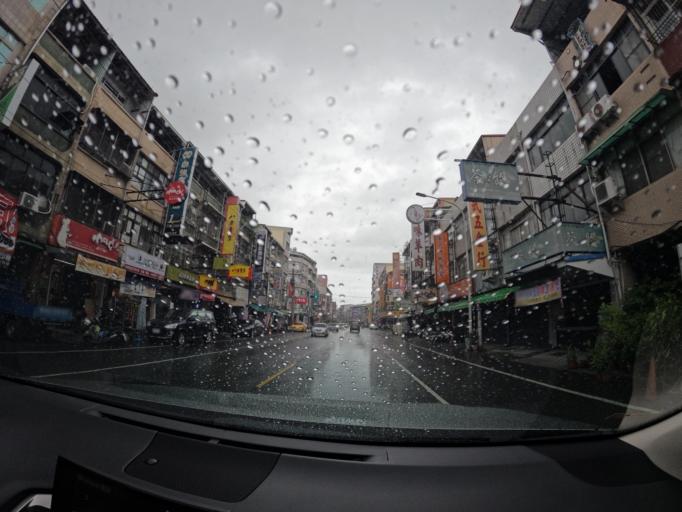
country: TW
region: Taiwan
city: Fengshan
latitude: 22.6371
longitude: 120.3643
